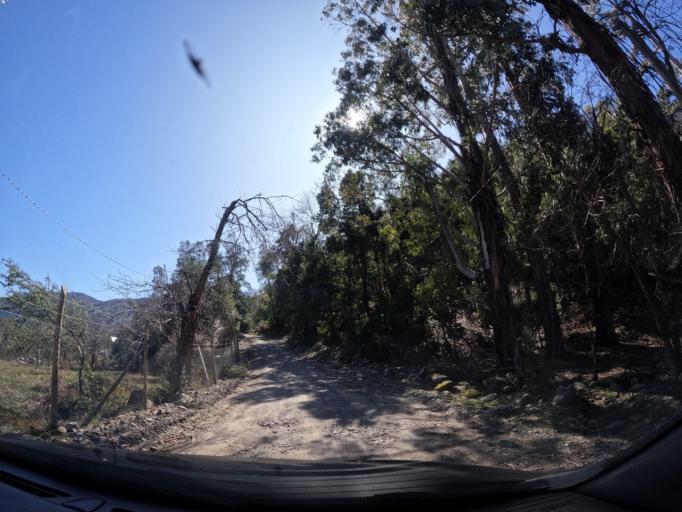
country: CL
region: Maule
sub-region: Provincia de Linares
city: Longavi
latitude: -36.2325
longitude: -71.3672
